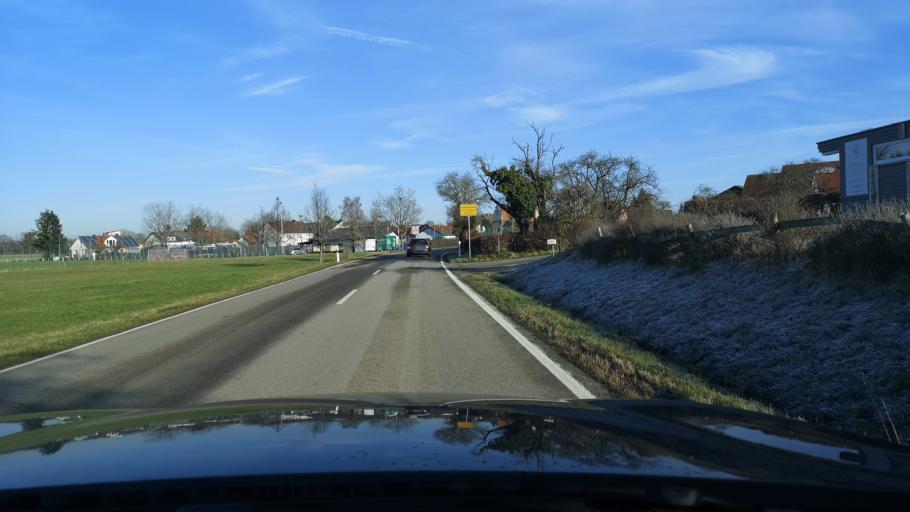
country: DE
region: Baden-Wuerttemberg
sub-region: Regierungsbezirk Stuttgart
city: Obergroningen
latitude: 48.8971
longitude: 9.9315
